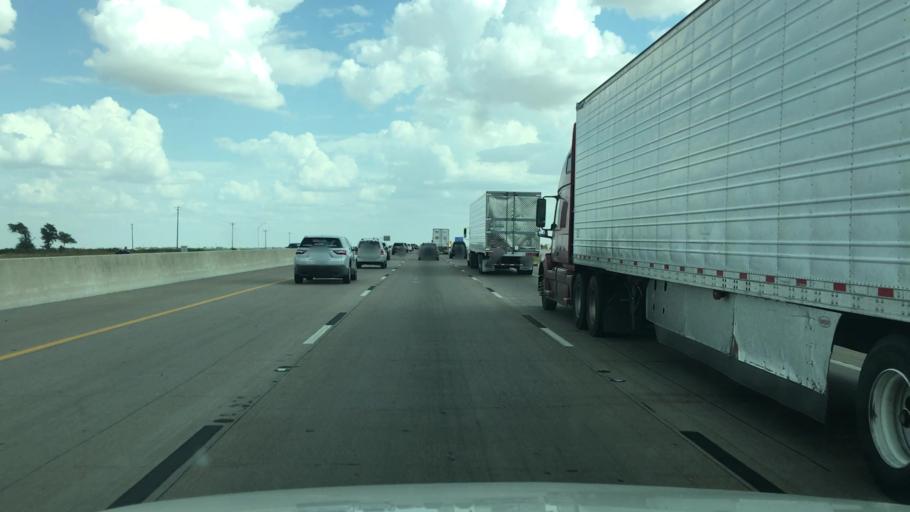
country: US
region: Texas
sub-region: Hill County
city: Hillsboro
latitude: 31.9481
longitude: -97.1115
